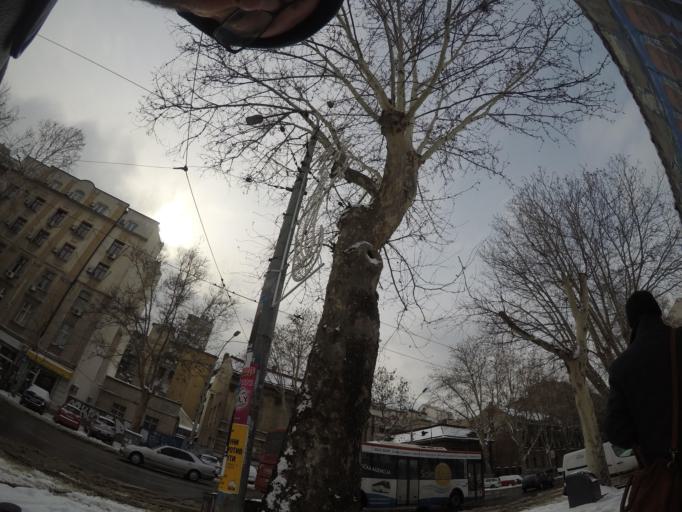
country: RS
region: Central Serbia
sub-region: Belgrade
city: Stari Grad
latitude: 44.8228
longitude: 20.4615
